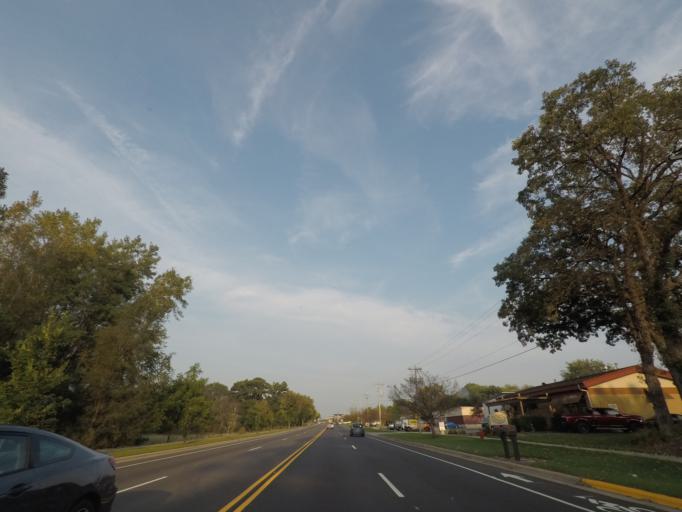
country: US
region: Wisconsin
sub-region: Dane County
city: Cottage Grove
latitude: 43.0867
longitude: -89.2046
